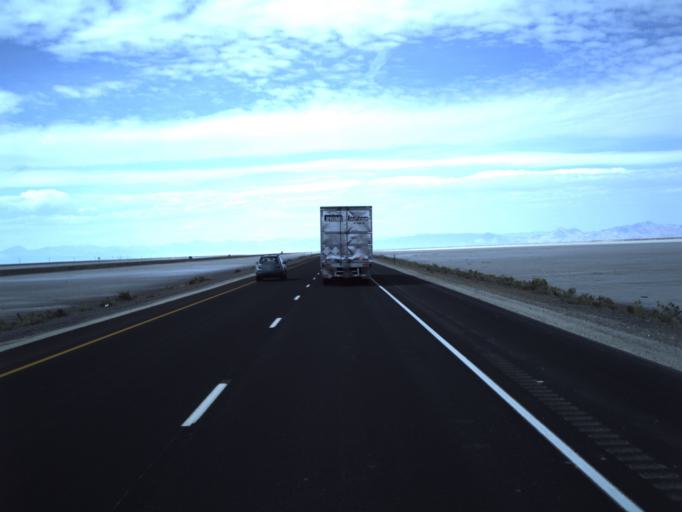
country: US
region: Utah
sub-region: Tooele County
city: Wendover
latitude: 40.7331
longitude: -113.5532
